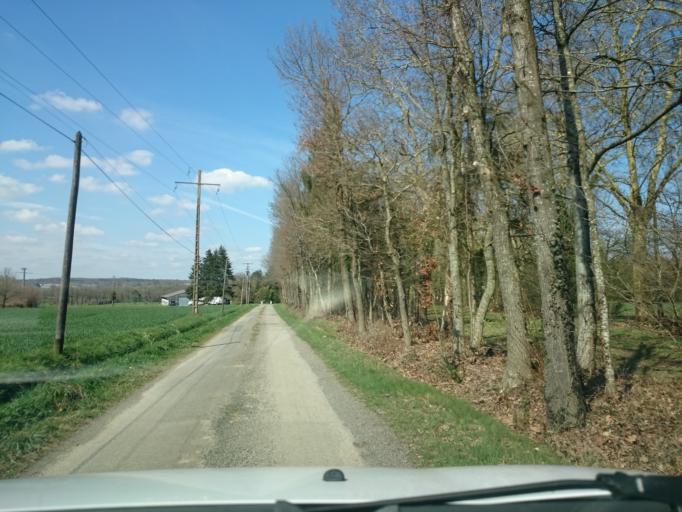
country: FR
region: Brittany
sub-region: Departement d'Ille-et-Vilaine
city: Acigne
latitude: 48.1638
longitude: -1.4974
